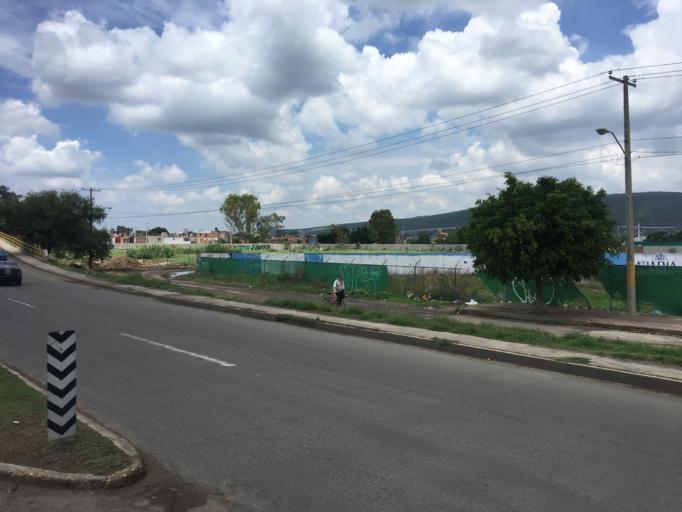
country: MX
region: Guanajuato
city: Irapuato
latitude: 20.7082
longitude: -101.3528
